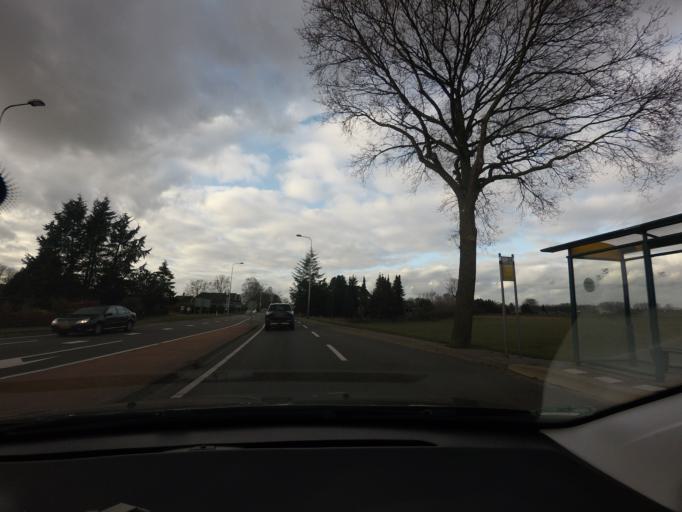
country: NL
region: Gelderland
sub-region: Gemeente Lochem
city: Epse
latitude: 52.2274
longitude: 6.1915
